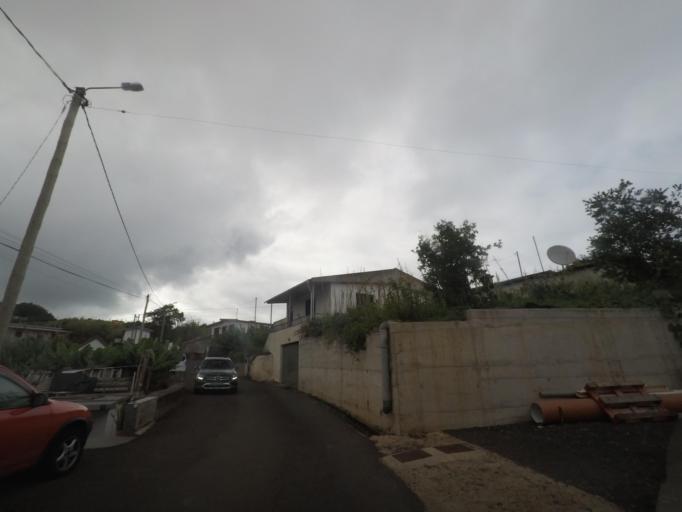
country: PT
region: Madeira
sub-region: Santana
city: Santana
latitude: 32.8311
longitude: -16.9104
